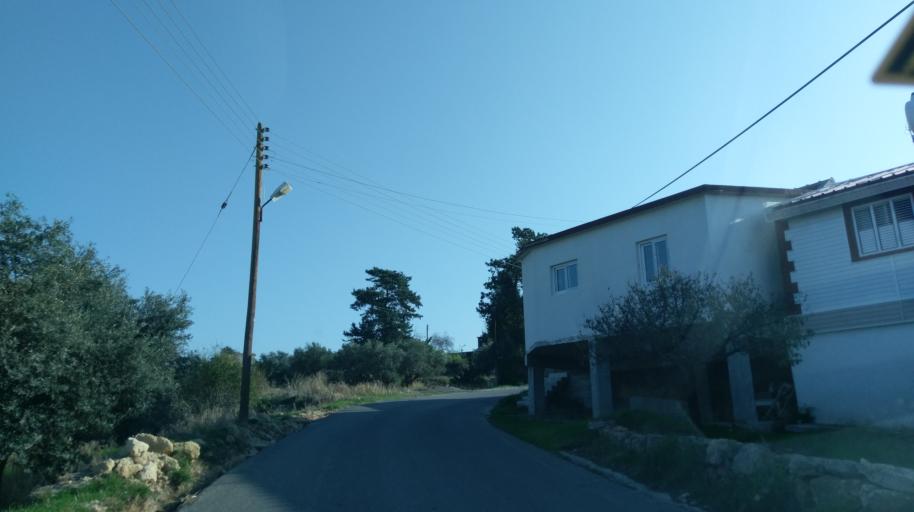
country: CY
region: Ammochostos
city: Leonarisso
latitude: 35.5382
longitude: 34.1909
